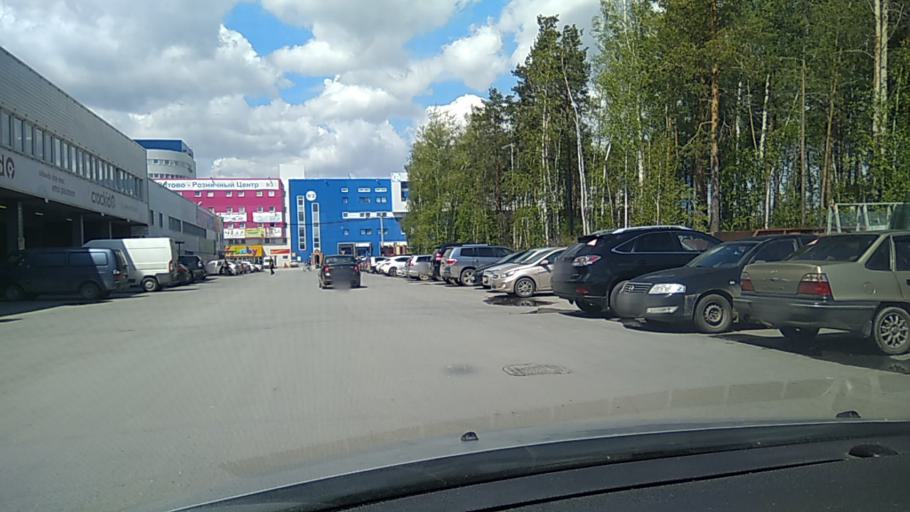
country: RU
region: Sverdlovsk
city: Istok
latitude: 56.7565
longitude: 60.7587
